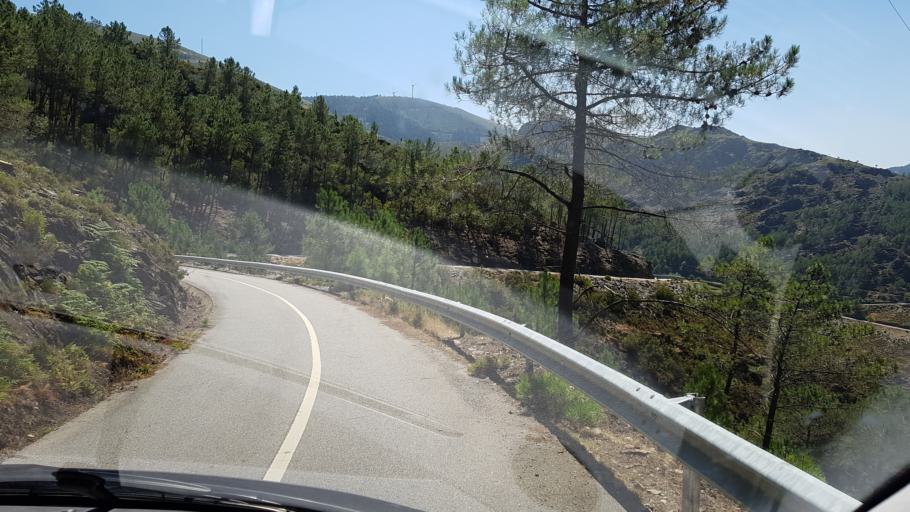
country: PT
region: Vila Real
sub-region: Mondim de Basto
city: Mondim de Basto
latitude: 41.3368
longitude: -7.8805
